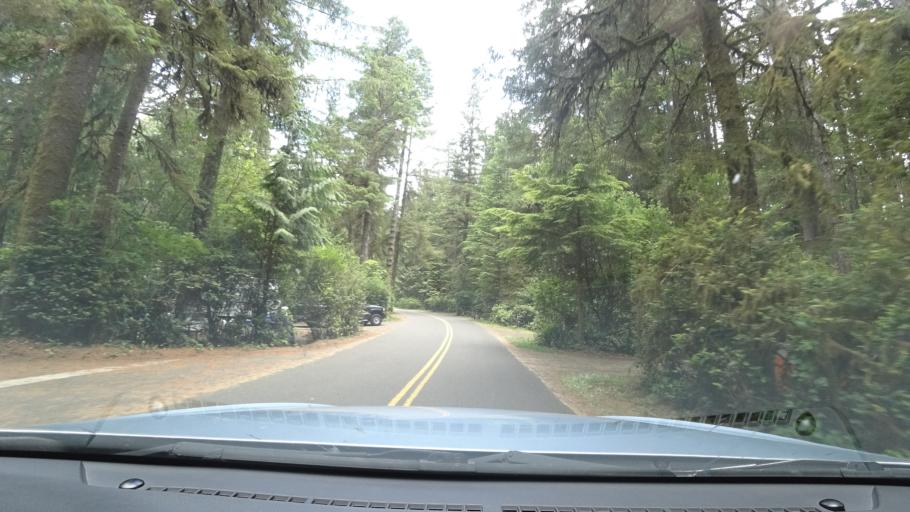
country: US
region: Oregon
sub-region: Lane County
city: Dunes City
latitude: 43.9235
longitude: -124.1106
